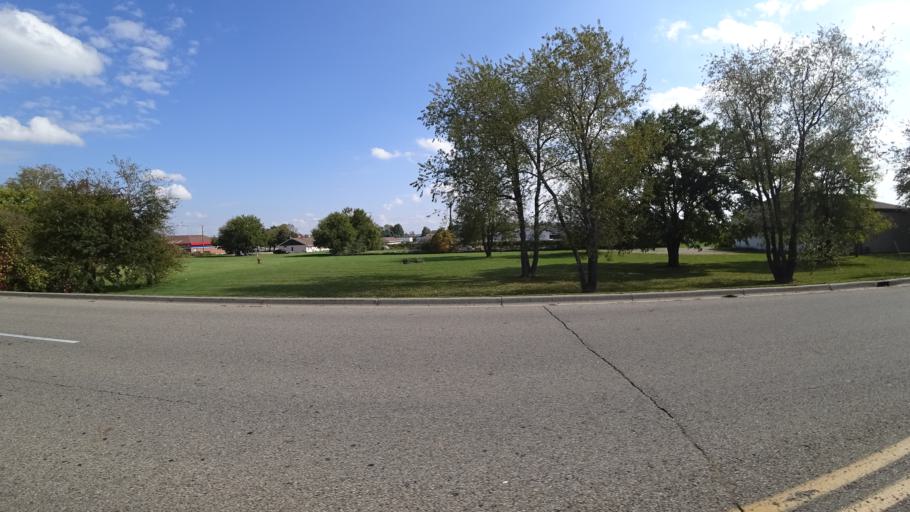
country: US
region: Michigan
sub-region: Saint Joseph County
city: Three Rivers
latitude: 41.9415
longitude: -85.6541
